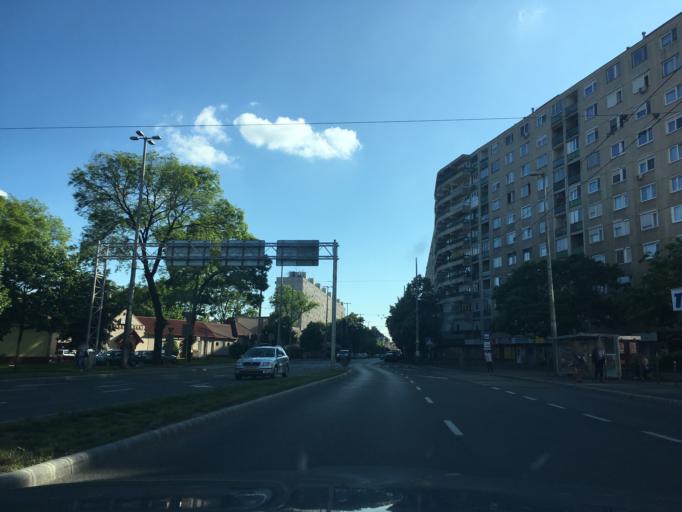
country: HU
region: Hajdu-Bihar
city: Debrecen
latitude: 47.5371
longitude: 21.6378
